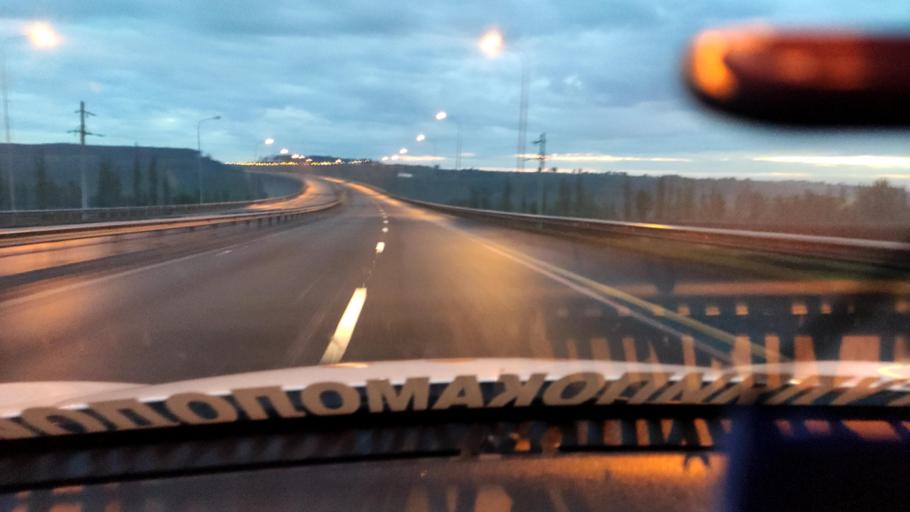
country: RU
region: Rostov
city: Tarasovskiy
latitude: 48.7248
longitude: 40.4053
